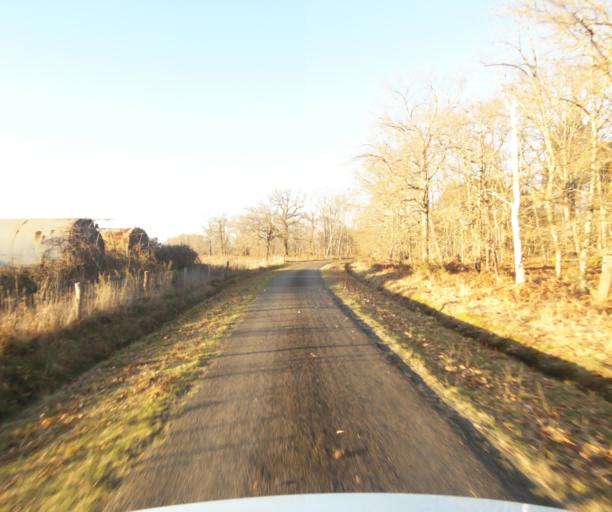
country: FR
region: Aquitaine
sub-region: Departement des Landes
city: Gabarret
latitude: 44.0999
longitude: -0.0296
